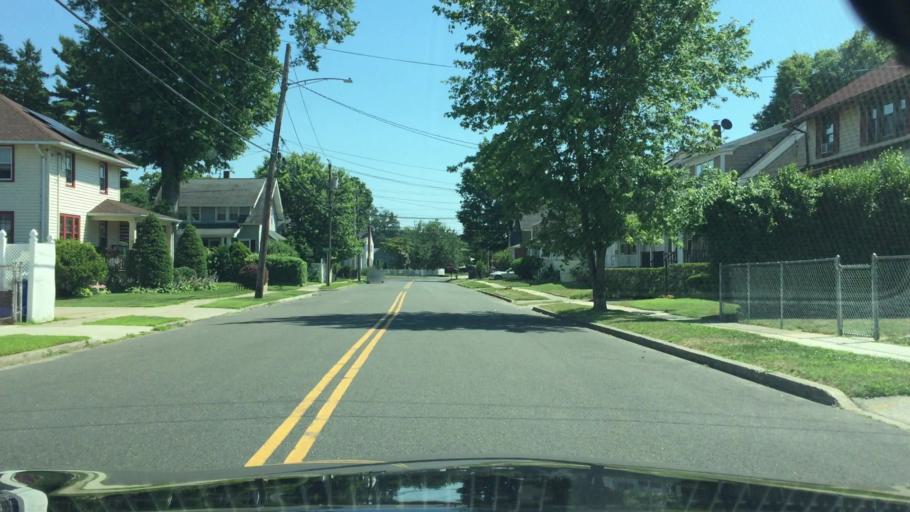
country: US
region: Connecticut
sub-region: Fairfield County
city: Stratford
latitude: 41.1838
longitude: -73.1344
